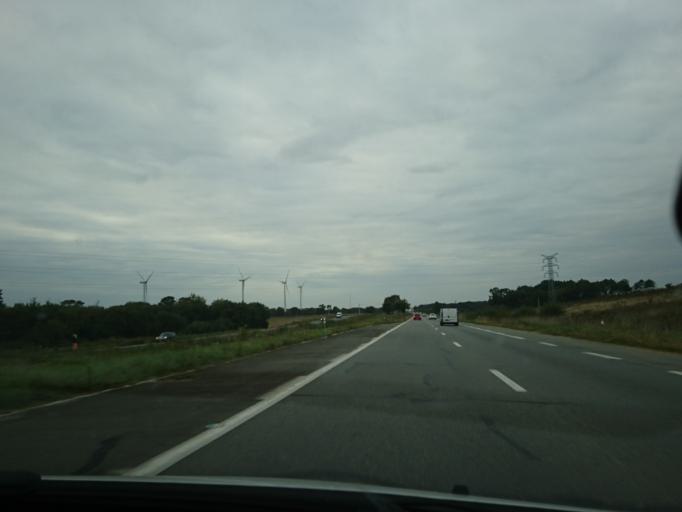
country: FR
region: Brittany
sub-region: Departement du Morbihan
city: Ambon
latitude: 47.5767
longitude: -2.5257
